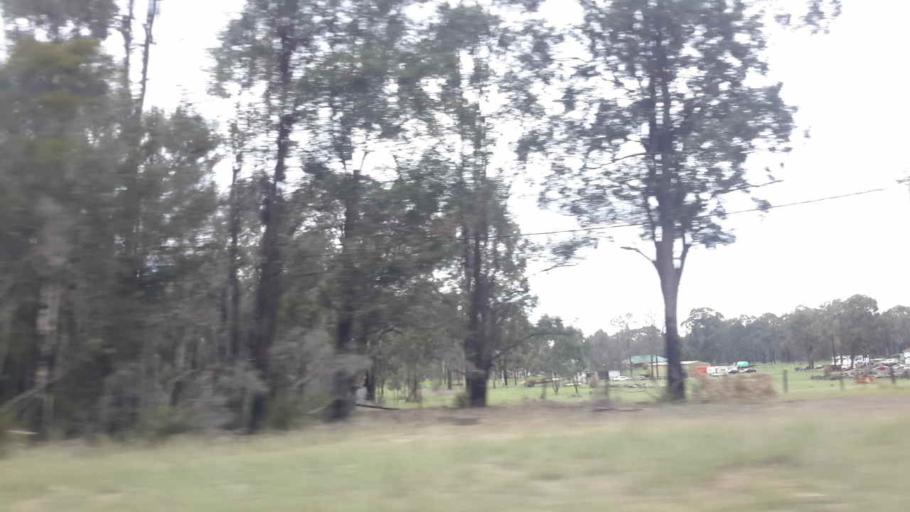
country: AU
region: New South Wales
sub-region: Penrith Municipality
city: Werrington Downs
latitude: -33.7020
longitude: 150.7251
